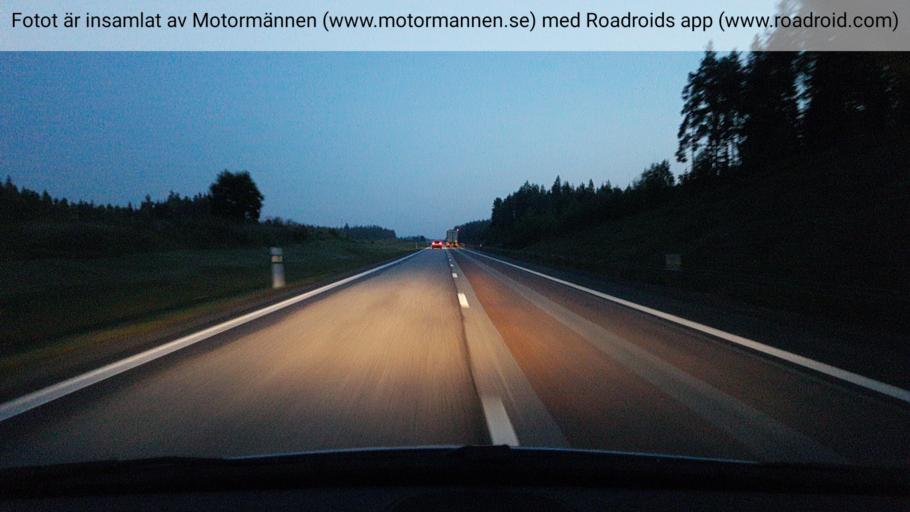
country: SE
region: Uppsala
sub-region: Tierps Kommun
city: Tierp
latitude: 60.2532
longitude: 17.5003
